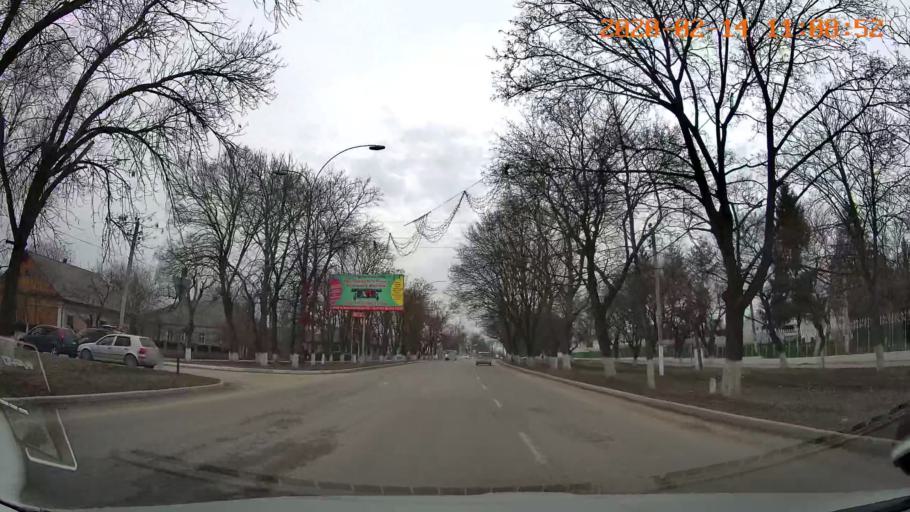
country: MD
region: Raionul Edinet
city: Edinet
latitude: 48.1746
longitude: 27.2983
